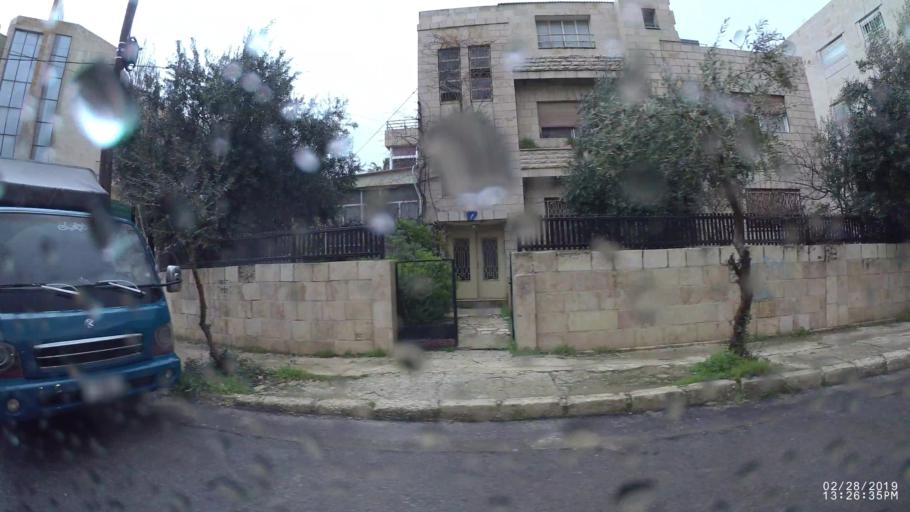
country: JO
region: Amman
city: Al Jubayhah
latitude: 32.0166
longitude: 35.8788
